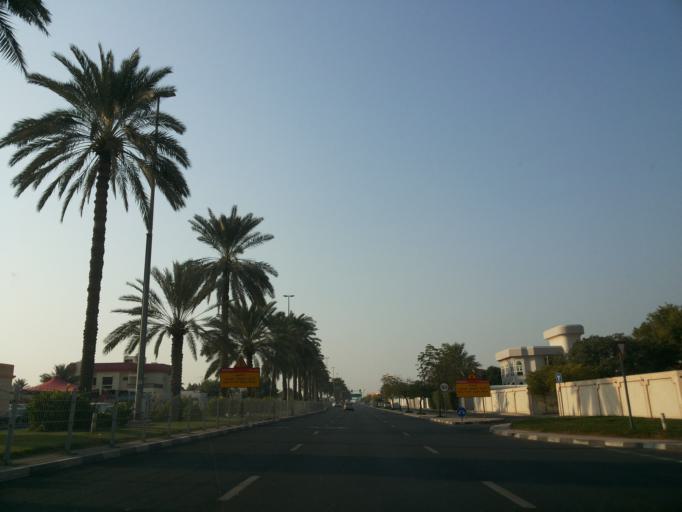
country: AE
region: Ash Shariqah
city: Sharjah
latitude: 25.2936
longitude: 55.3416
